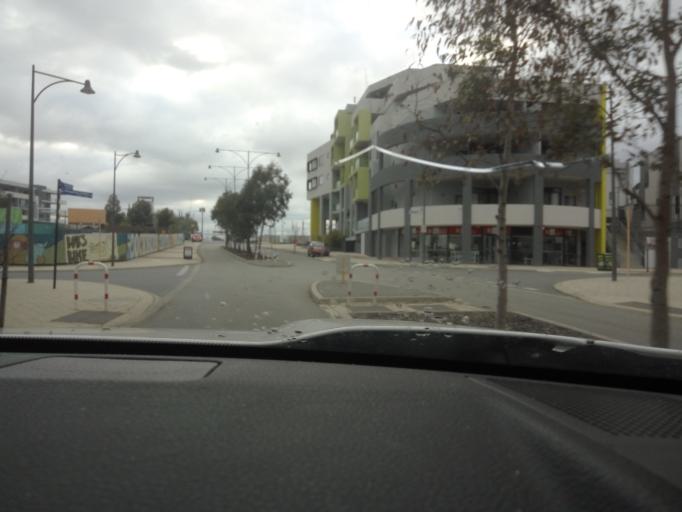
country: AU
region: Western Australia
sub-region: City of Cockburn
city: Success
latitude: -32.1263
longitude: 115.8556
